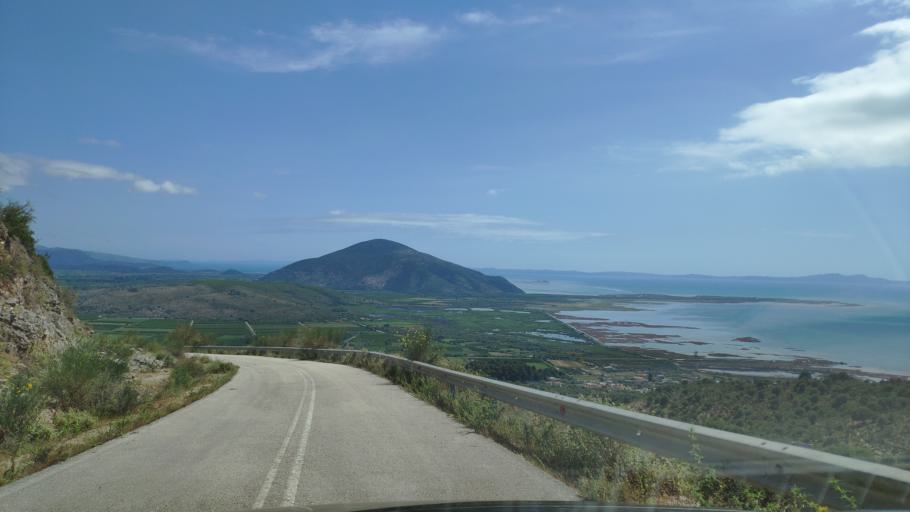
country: AL
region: Vlore
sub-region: Rrethi i Sarandes
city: Konispol
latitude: 39.6341
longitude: 20.2057
